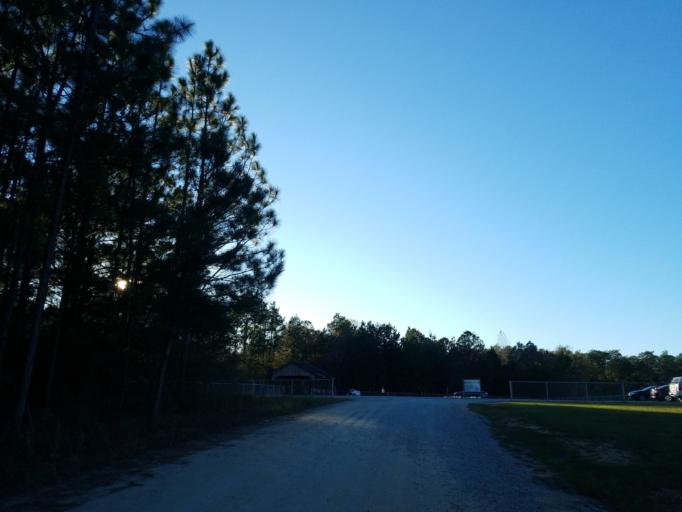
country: US
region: Mississippi
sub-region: Lamar County
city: Arnold Line
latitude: 31.3440
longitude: -89.4009
